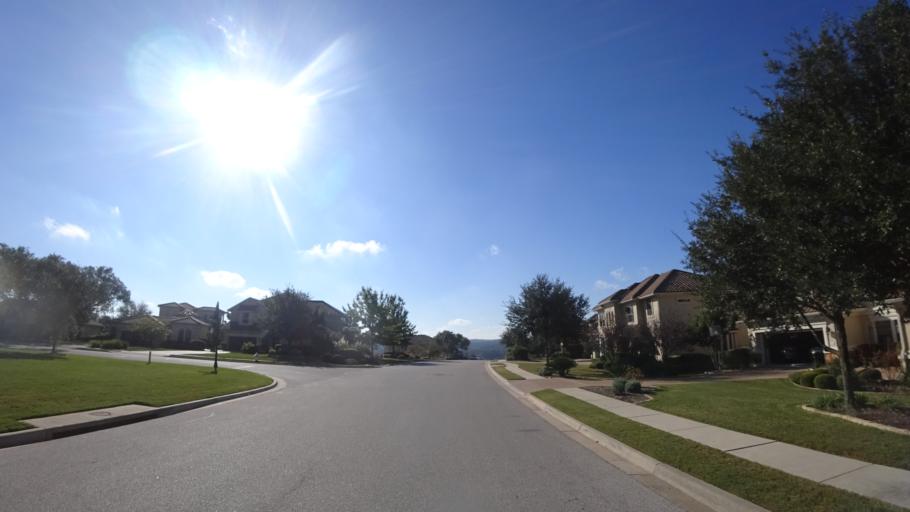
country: US
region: Texas
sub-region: Travis County
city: Bee Cave
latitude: 30.3469
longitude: -97.8940
